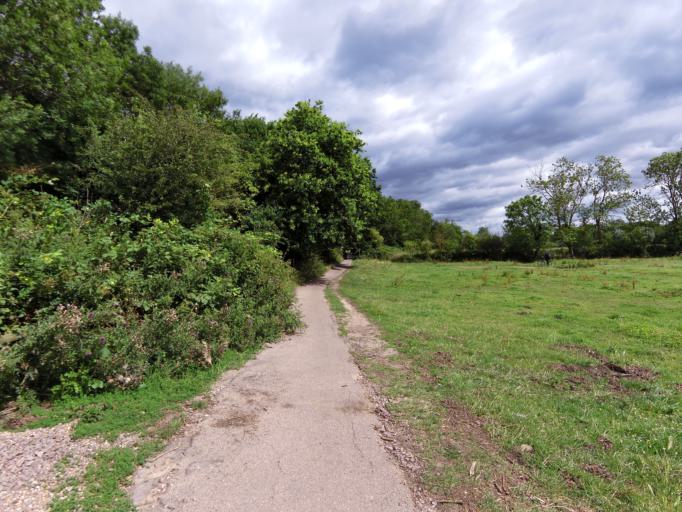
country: GB
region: England
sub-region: Cambridgeshire
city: Grantchester
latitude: 52.1907
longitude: 0.1034
